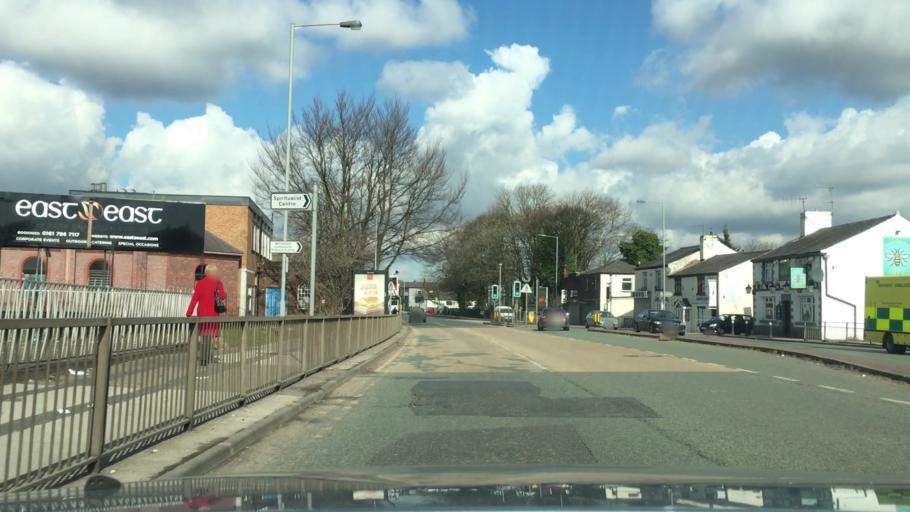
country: GB
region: England
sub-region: Borough of Bury
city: Whitefield
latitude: 53.5443
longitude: -2.2910
